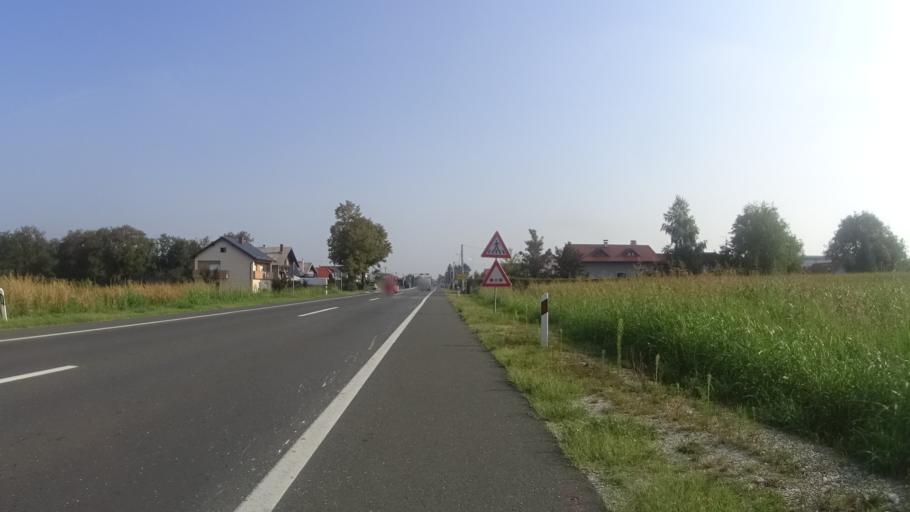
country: HR
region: Varazdinska
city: Varazdin
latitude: 46.3361
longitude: 16.3610
